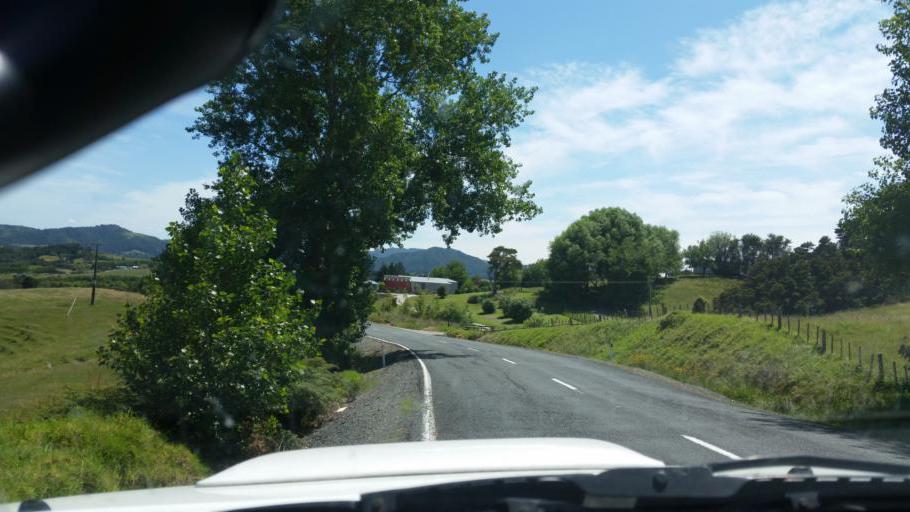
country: NZ
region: Auckland
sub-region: Auckland
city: Wellsford
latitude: -36.1815
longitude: 174.4122
